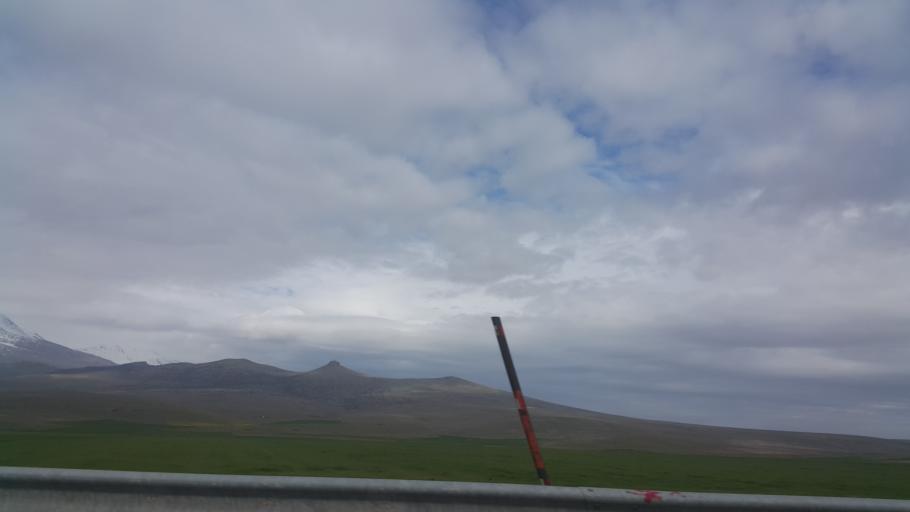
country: TR
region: Aksaray
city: Taspinar
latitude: 38.0539
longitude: 34.0321
